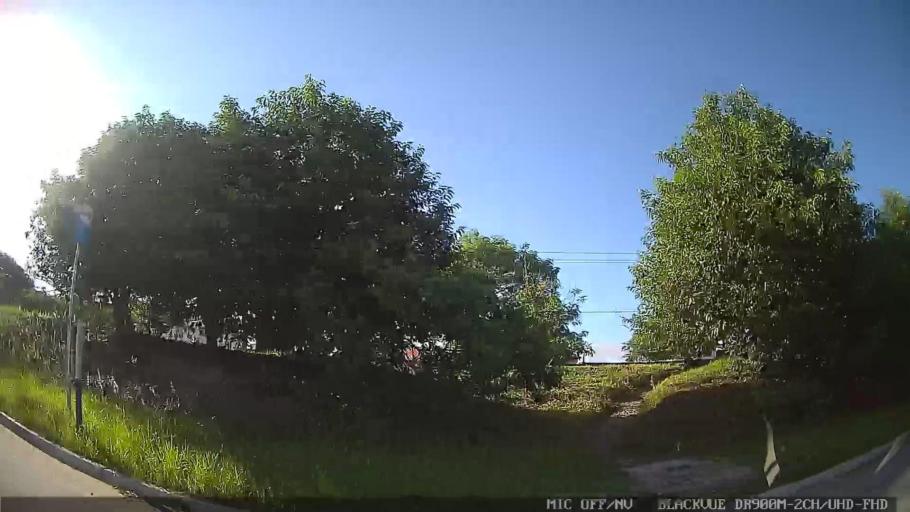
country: BR
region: Sao Paulo
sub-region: Peruibe
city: Peruibe
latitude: -24.2964
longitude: -46.9807
